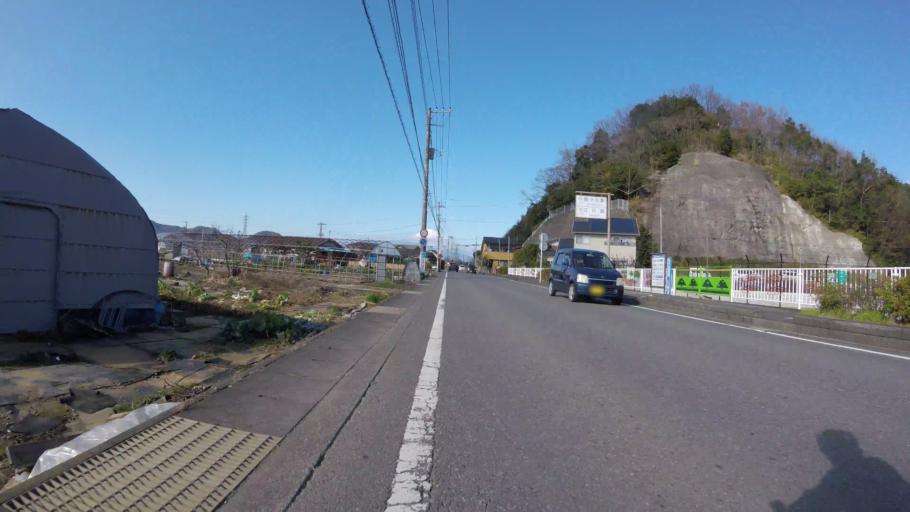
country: JP
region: Shizuoka
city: Mishima
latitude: 35.0453
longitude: 138.9554
